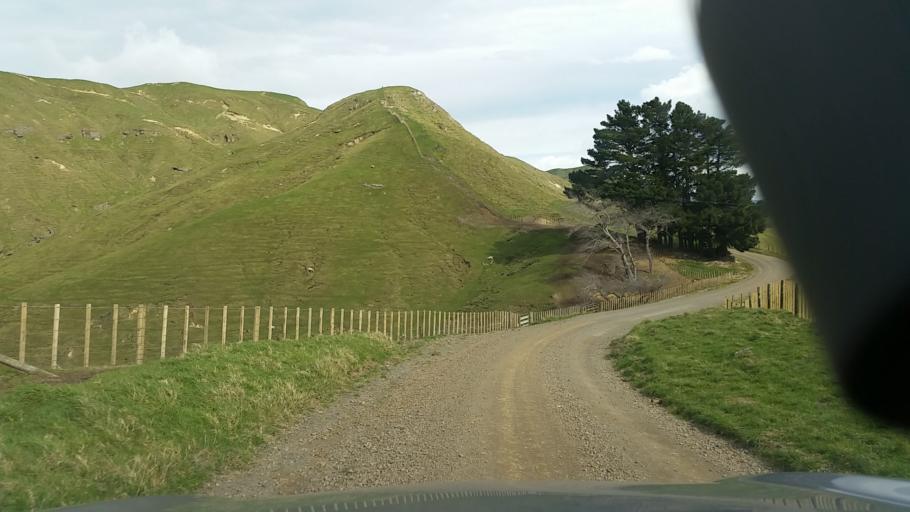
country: NZ
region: Hawke's Bay
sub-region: Napier City
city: Napier
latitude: -39.2040
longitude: 176.9414
